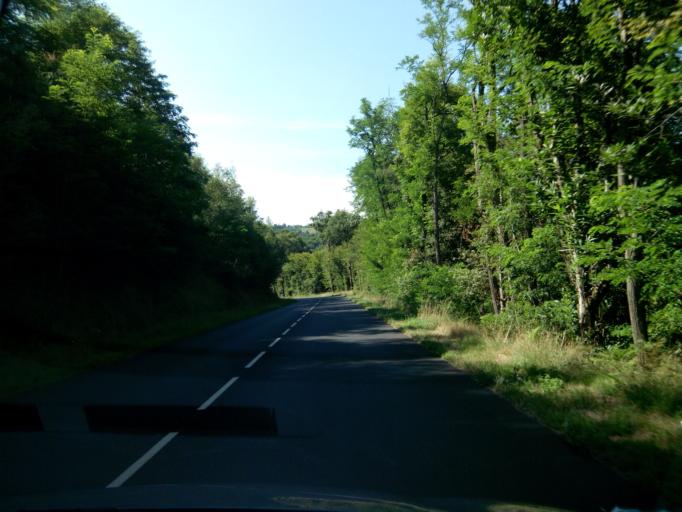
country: FR
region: Limousin
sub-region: Departement de la Correze
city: Beynat
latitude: 45.1277
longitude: 1.6847
